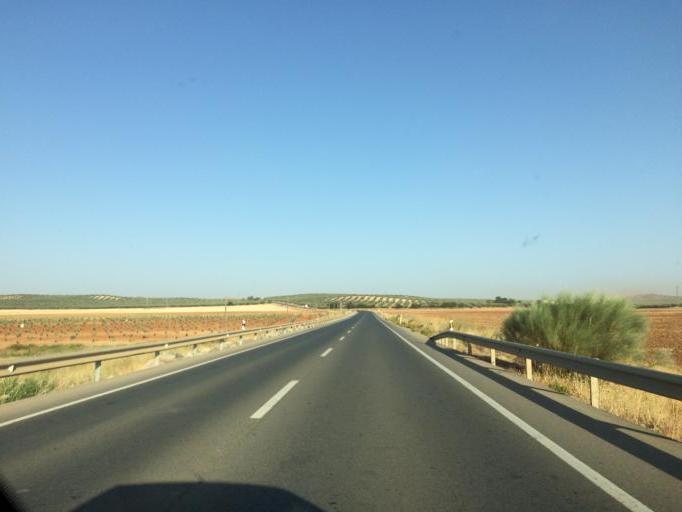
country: ES
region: Andalusia
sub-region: Provincia de Malaga
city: Humilladero
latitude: 37.0527
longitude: -4.7589
